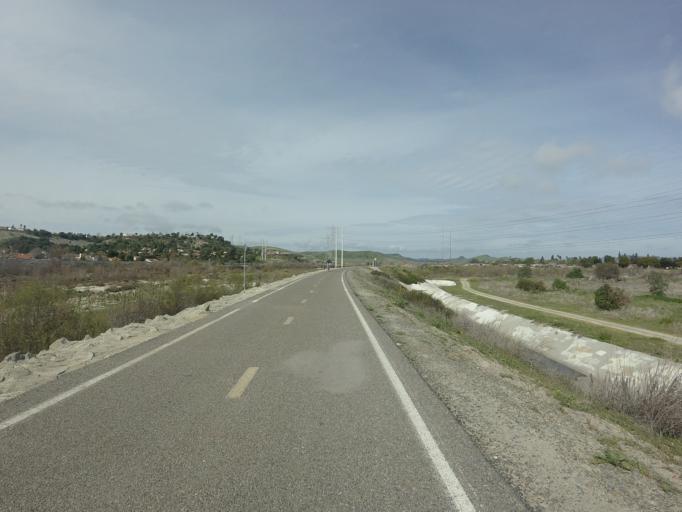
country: US
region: California
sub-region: San Diego County
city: Camp Pendleton South
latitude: 33.2277
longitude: -117.3431
